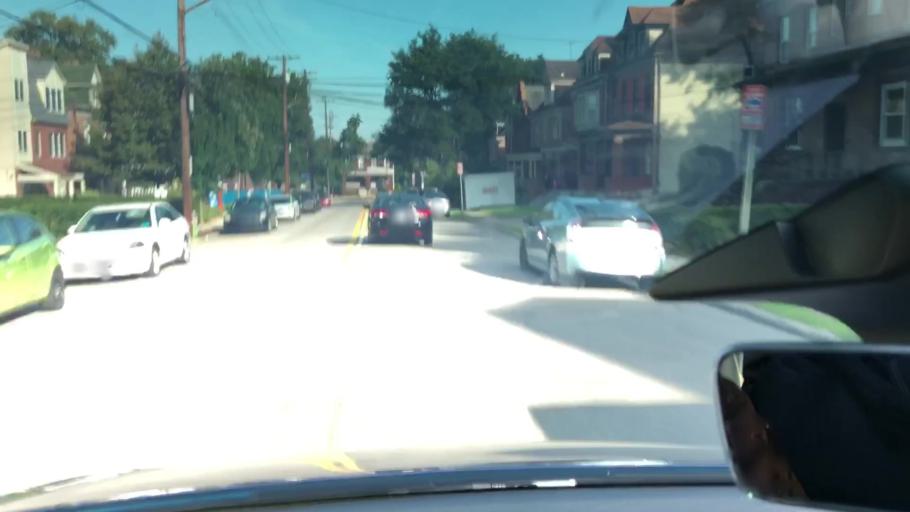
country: US
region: Pennsylvania
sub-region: Allegheny County
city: Bloomfield
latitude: 40.4693
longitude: -79.9291
